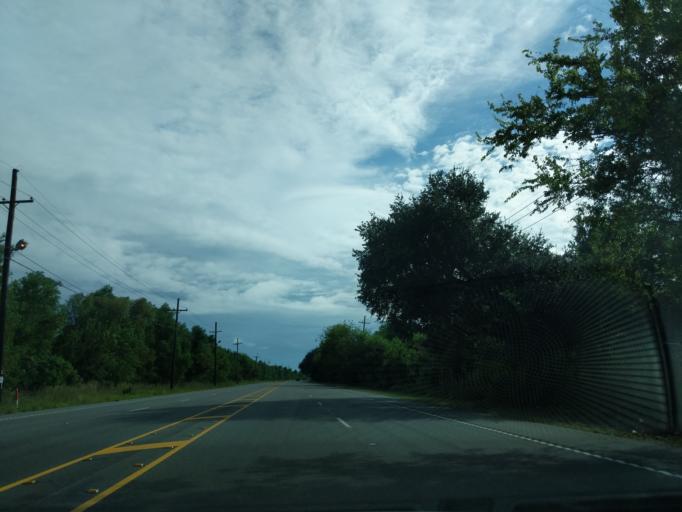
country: US
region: Louisiana
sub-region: Saint Bernard Parish
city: Meraux
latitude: 30.0699
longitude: -89.8641
